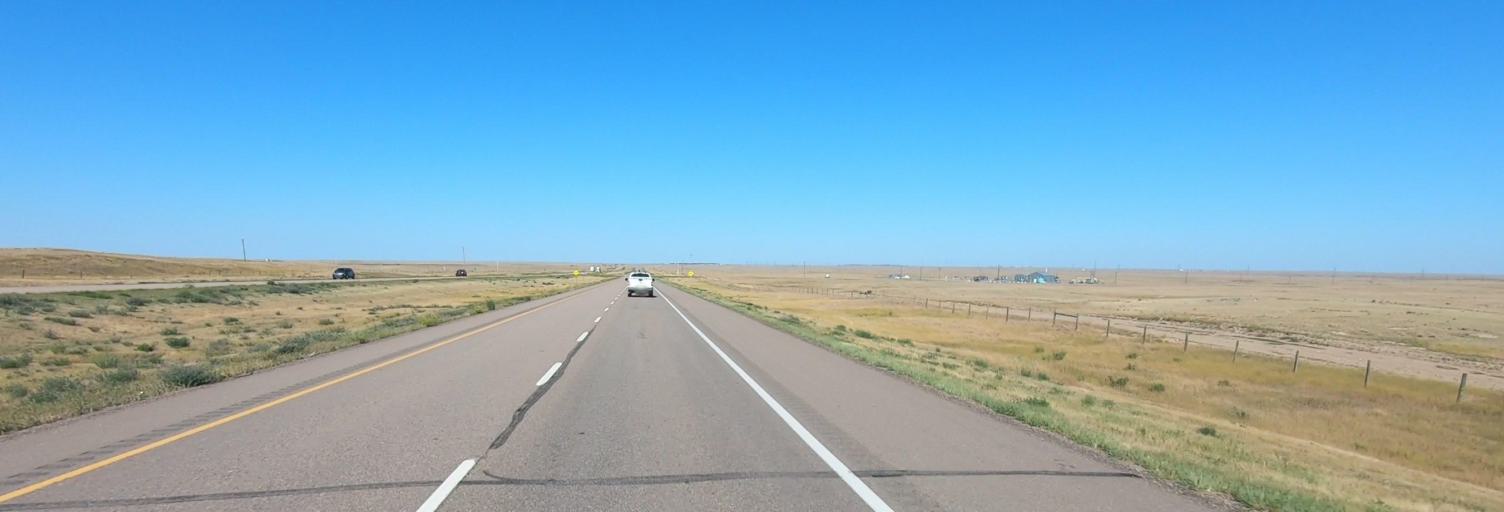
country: CA
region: Alberta
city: Medicine Hat
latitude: 50.1831
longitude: -111.0455
